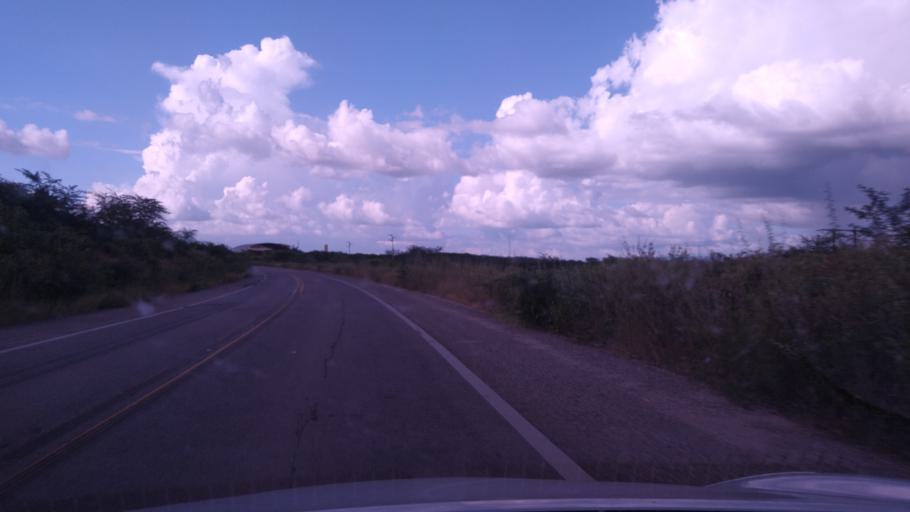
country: BR
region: Ceara
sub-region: Caninde
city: Caninde
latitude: -4.3954
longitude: -39.3152
